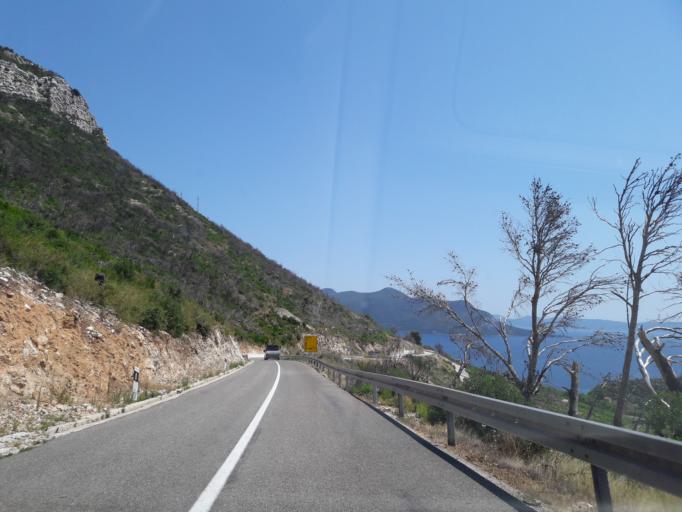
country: HR
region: Dubrovacko-Neretvanska
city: Blato
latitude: 42.9199
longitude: 17.4087
